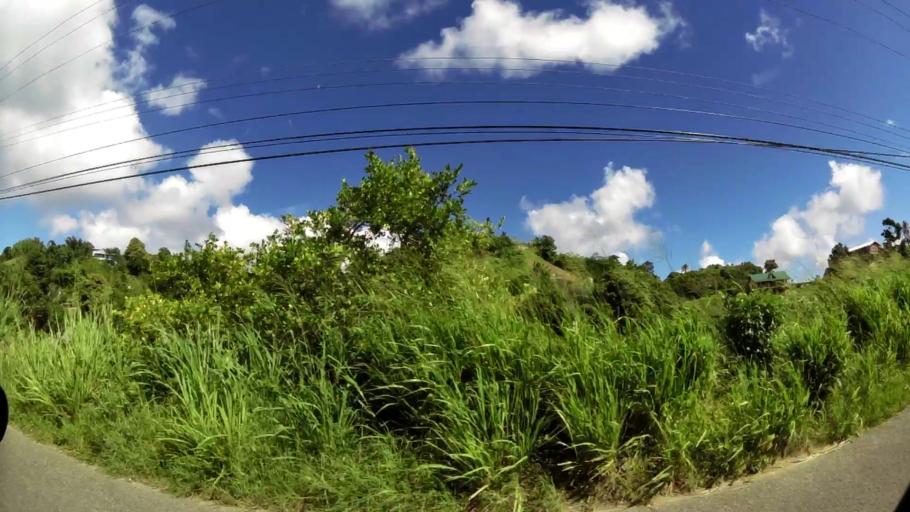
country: TT
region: Tobago
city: Scarborough
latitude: 11.2388
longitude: -60.7362
